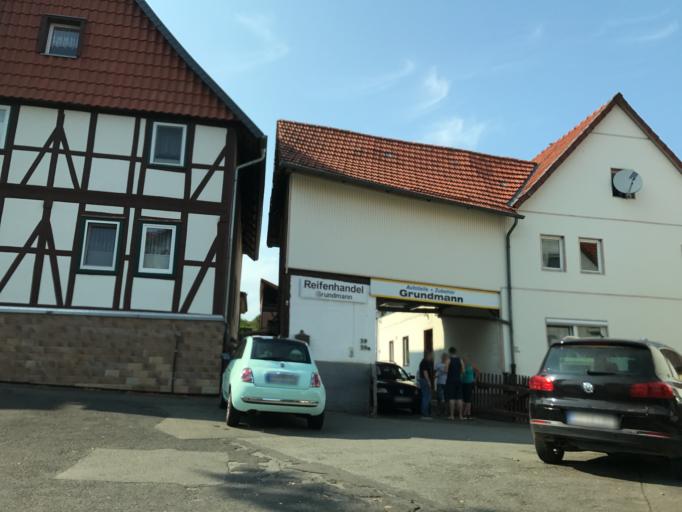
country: DE
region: Lower Saxony
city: Ebergotzen
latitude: 51.5718
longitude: 10.1072
